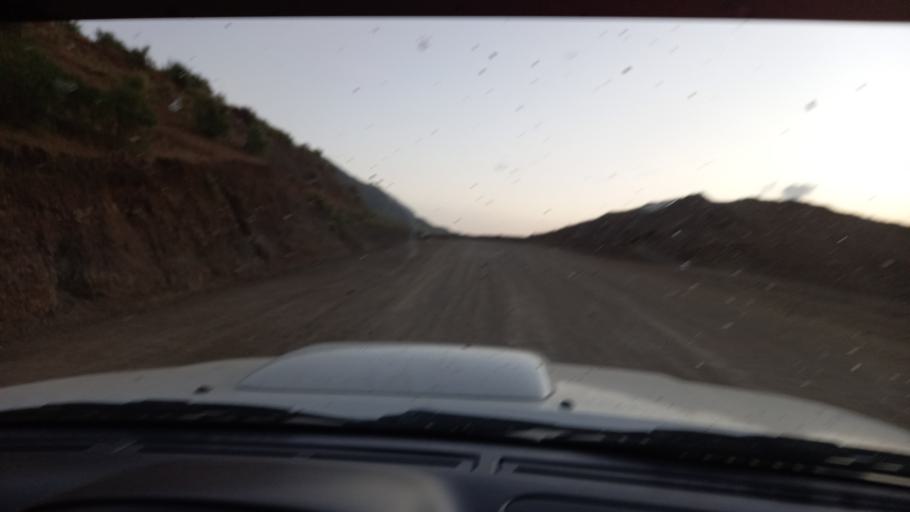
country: ET
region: Amhara
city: Debark'
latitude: 13.0337
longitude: 38.0539
